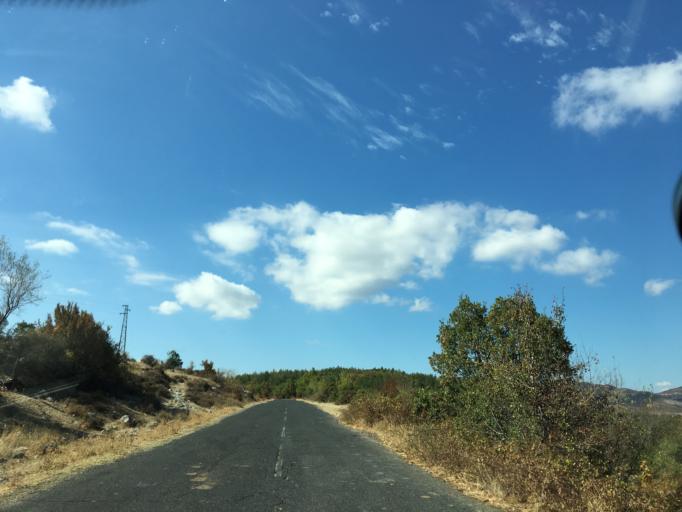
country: BG
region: Kurdzhali
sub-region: Obshtina Krumovgrad
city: Krumovgrad
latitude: 41.5472
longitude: 25.5304
